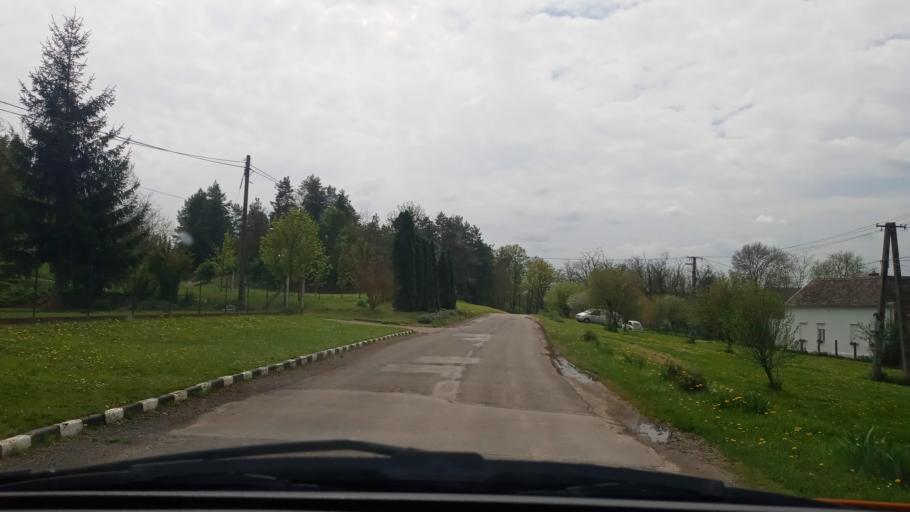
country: HU
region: Baranya
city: Sasd
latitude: 46.2637
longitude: 18.1239
